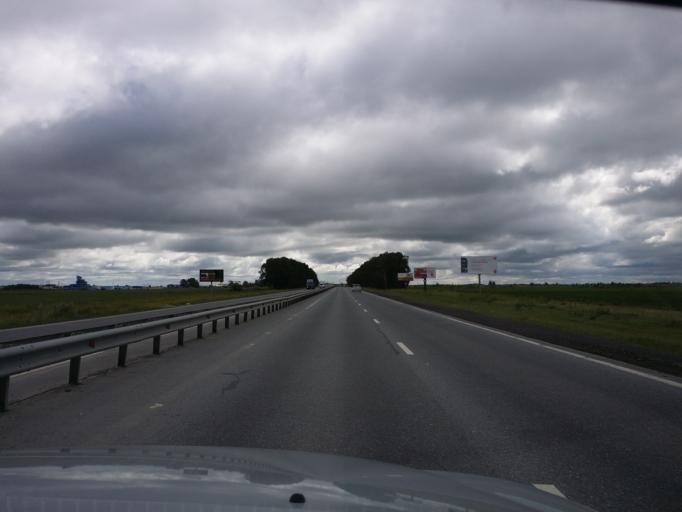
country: RU
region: Tjumen
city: Antipino
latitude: 57.1594
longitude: 65.8267
